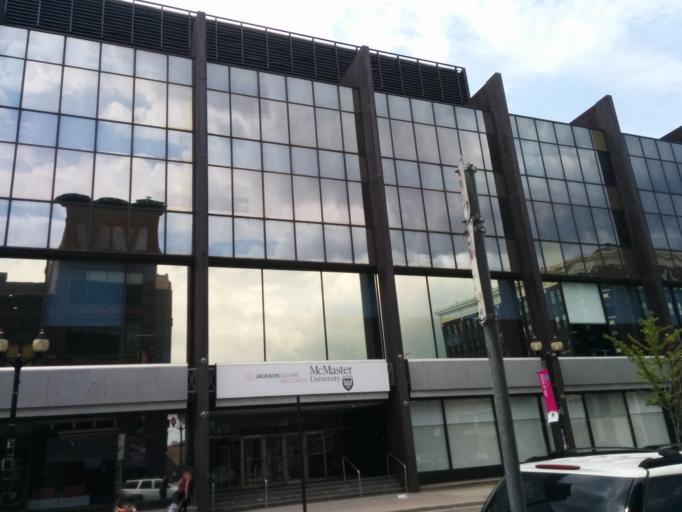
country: CA
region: Ontario
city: Hamilton
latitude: 43.2573
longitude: -79.8689
